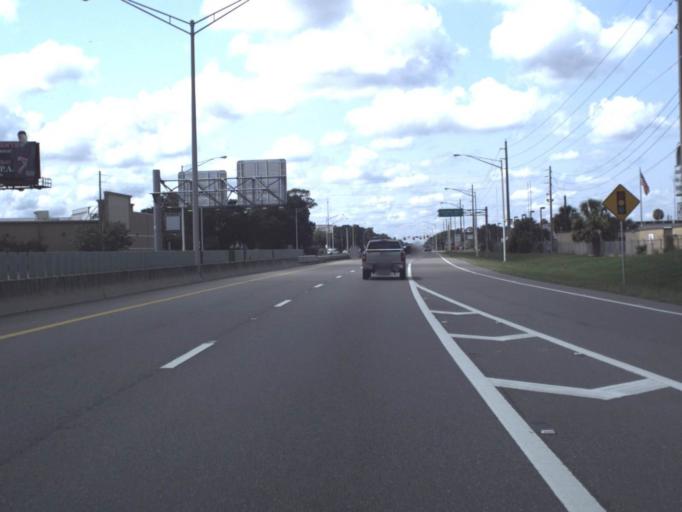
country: US
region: Florida
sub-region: Duval County
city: Jacksonville
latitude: 30.3201
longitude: -81.5590
